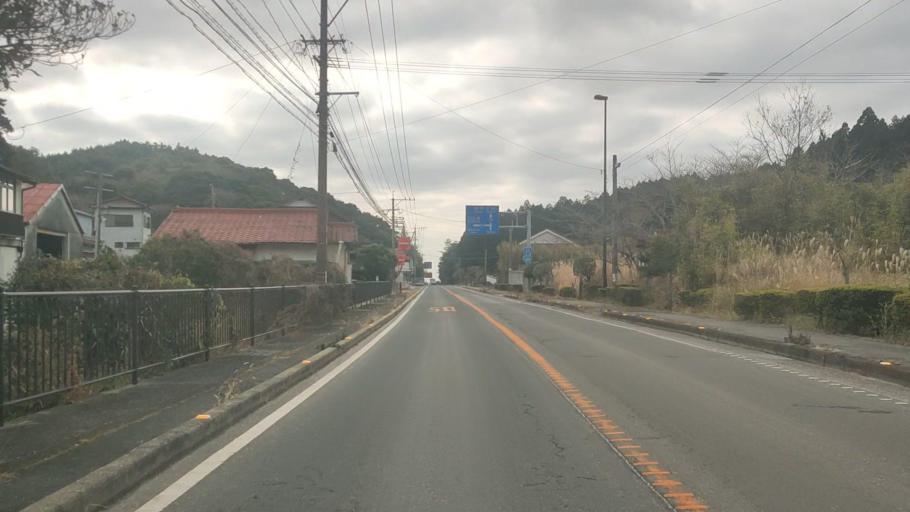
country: JP
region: Nagasaki
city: Shimabara
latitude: 32.7270
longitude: 130.2536
